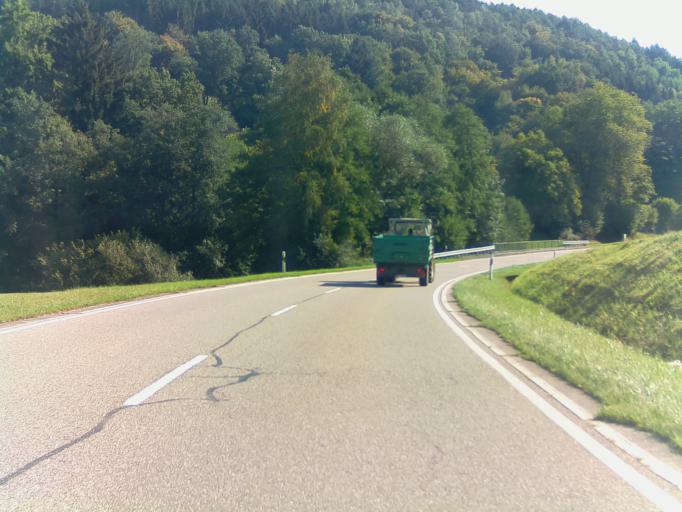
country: DE
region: Baden-Wuerttemberg
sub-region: Karlsruhe Region
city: Heddesbach
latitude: 49.4747
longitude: 8.8371
